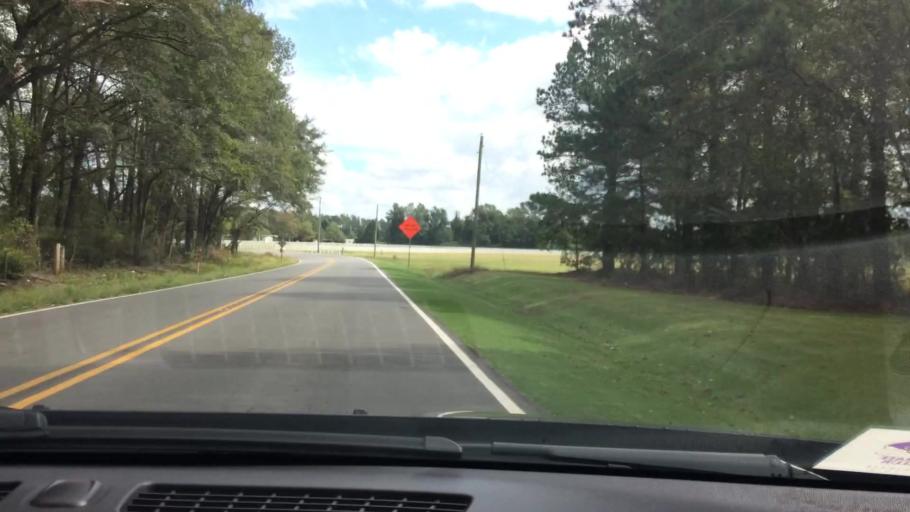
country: US
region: North Carolina
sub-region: Pitt County
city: Ayden
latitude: 35.4559
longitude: -77.4825
